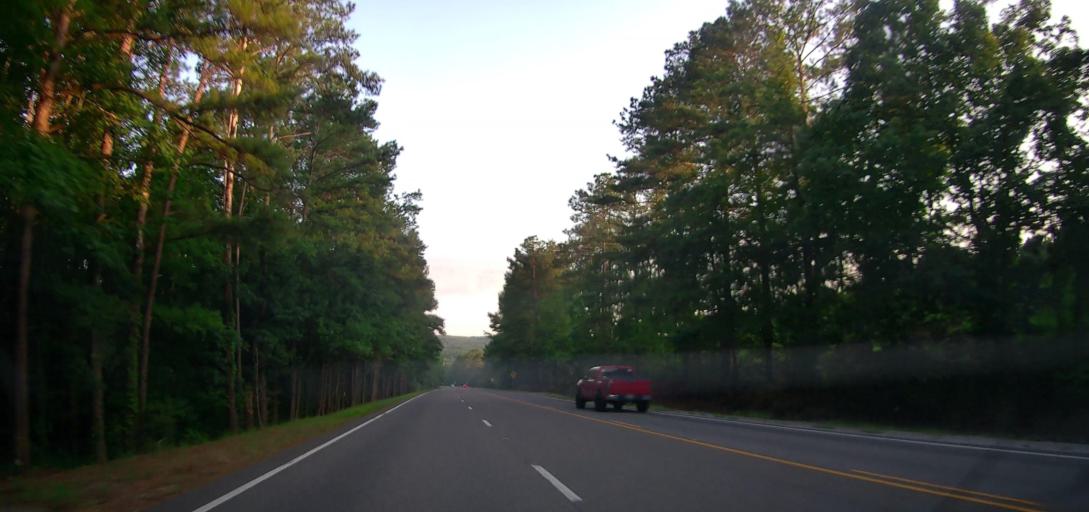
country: US
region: Alabama
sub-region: Marion County
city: Hamilton
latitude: 34.0792
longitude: -87.9765
